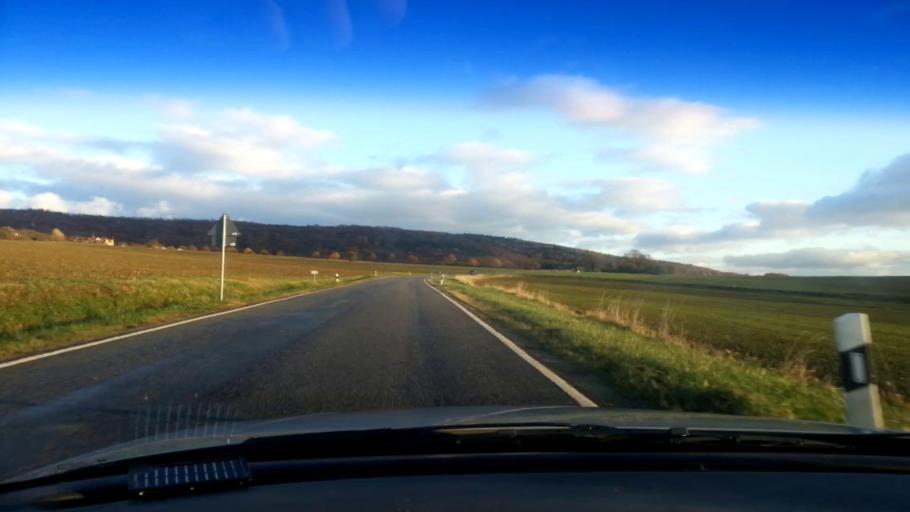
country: DE
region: Bavaria
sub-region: Upper Franconia
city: Buttenheim
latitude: 49.8423
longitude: 11.0241
